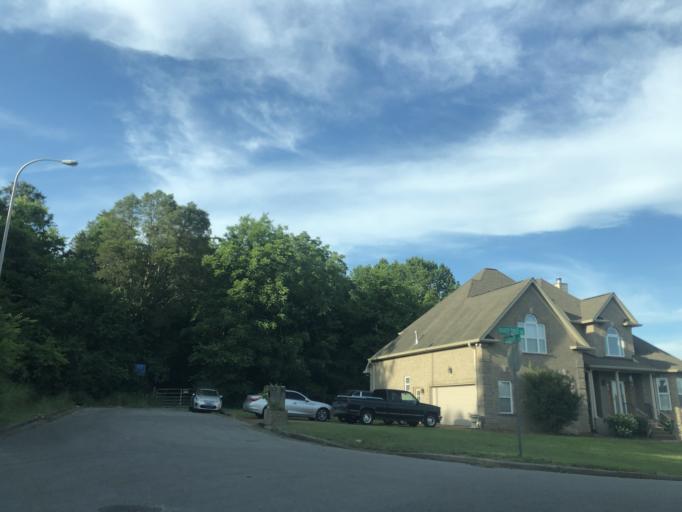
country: US
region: Tennessee
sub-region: Davidson County
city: Nashville
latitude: 36.2200
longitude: -86.8537
